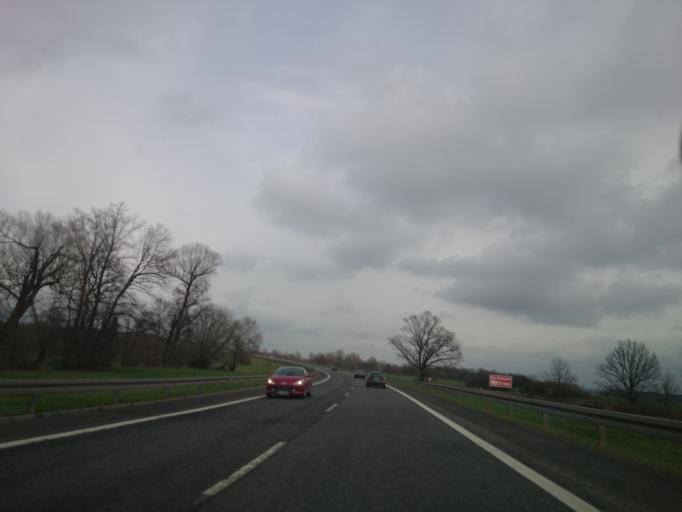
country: PL
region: Opole Voivodeship
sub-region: Powiat nyski
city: Otmuchow
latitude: 50.4564
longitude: 17.1815
